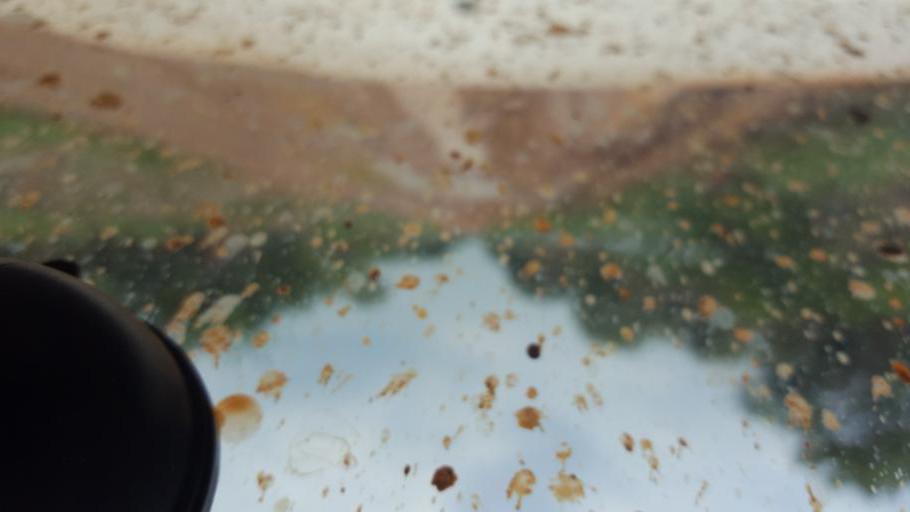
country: CD
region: Bandundu
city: Bandundu
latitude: -3.7593
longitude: 17.1533
